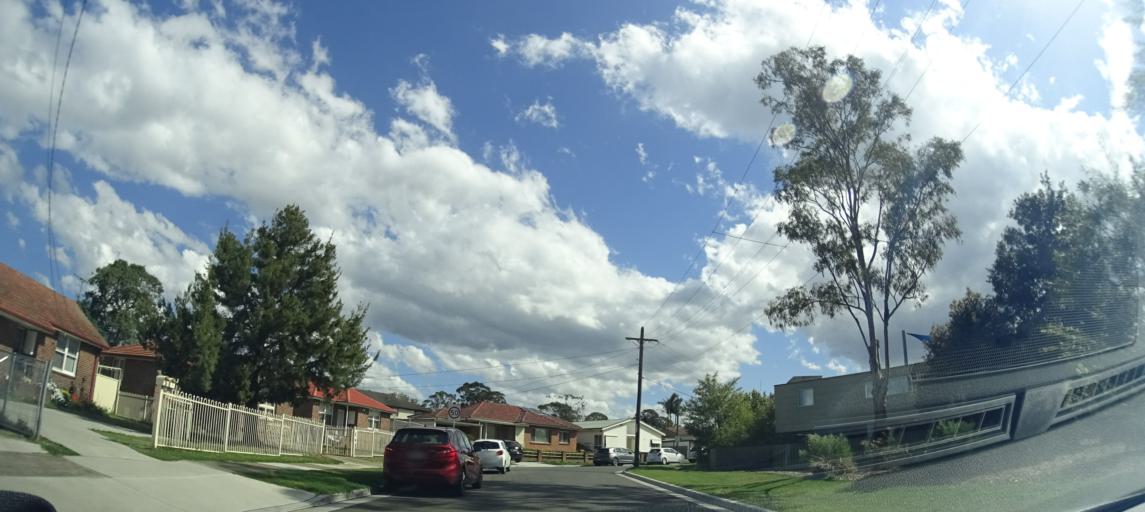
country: AU
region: New South Wales
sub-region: Bankstown
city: Revesby
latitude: -33.9541
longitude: 151.0142
